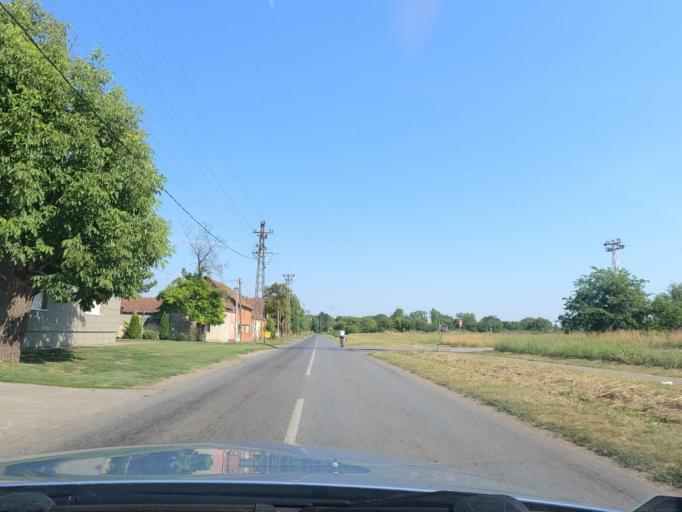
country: RS
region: Autonomna Pokrajina Vojvodina
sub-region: Juznobacki Okrug
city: Becej
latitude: 45.6242
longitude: 20.0309
